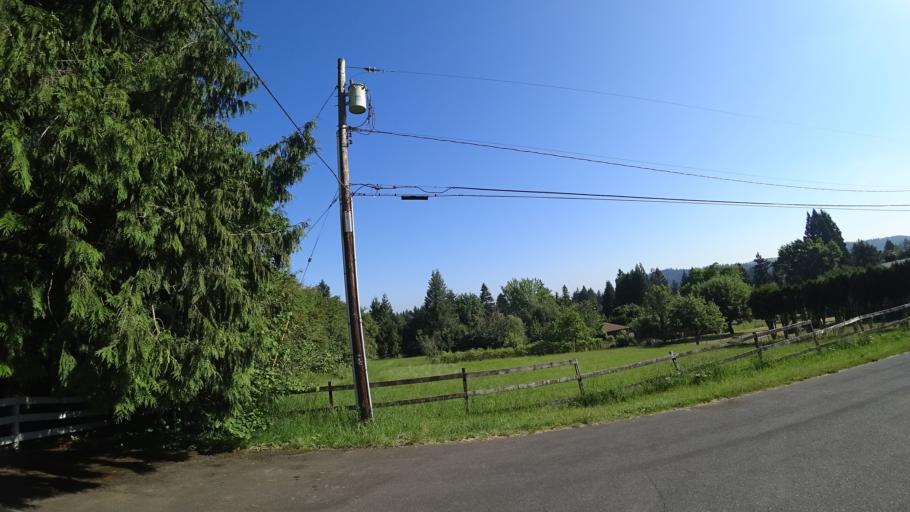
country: US
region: Oregon
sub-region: Clackamas County
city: Happy Valley
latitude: 45.4704
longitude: -122.5336
